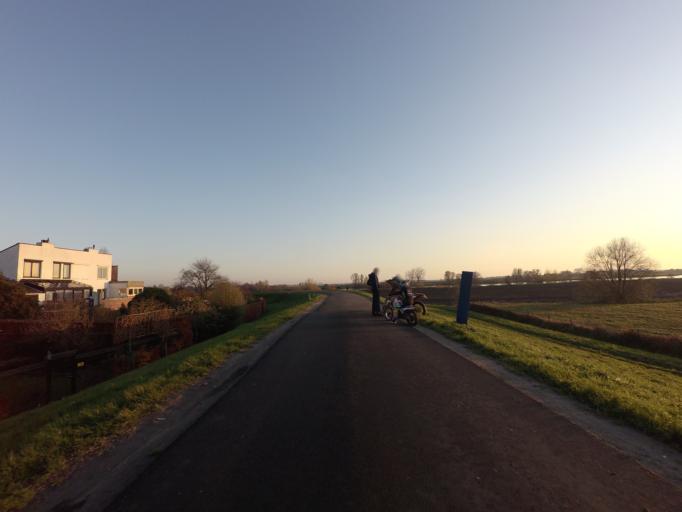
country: NL
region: Gelderland
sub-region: Gemeente Zaltbommel
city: Nederhemert-Noord
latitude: 51.7463
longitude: 5.2125
